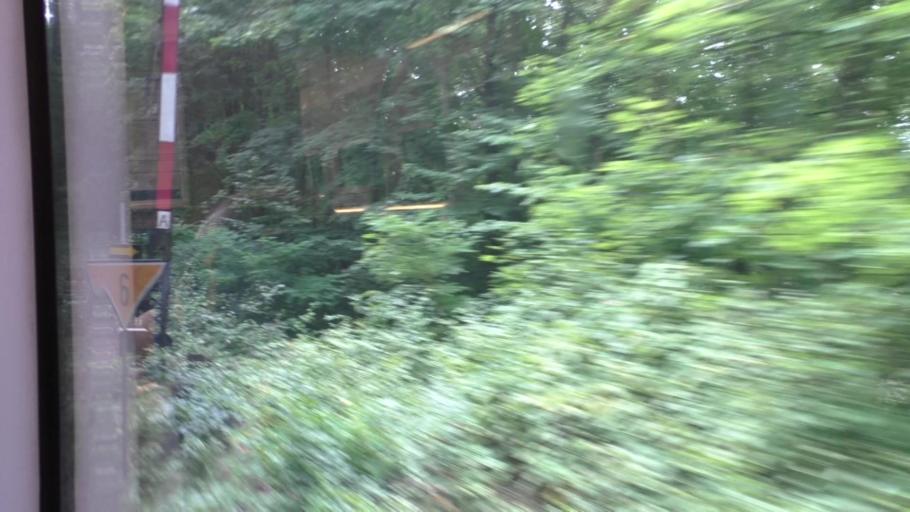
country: DE
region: Saxony
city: Hirschfelde
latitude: 50.9533
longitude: 14.8962
